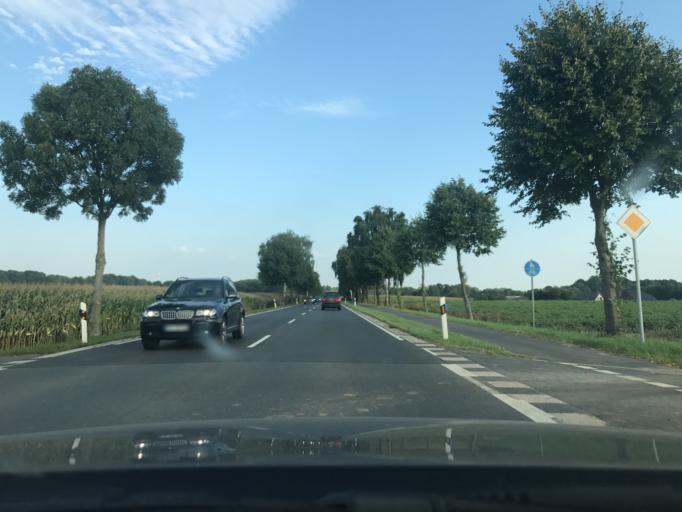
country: DE
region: North Rhine-Westphalia
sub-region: Regierungsbezirk Dusseldorf
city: Rheurdt
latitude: 51.4181
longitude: 6.4681
